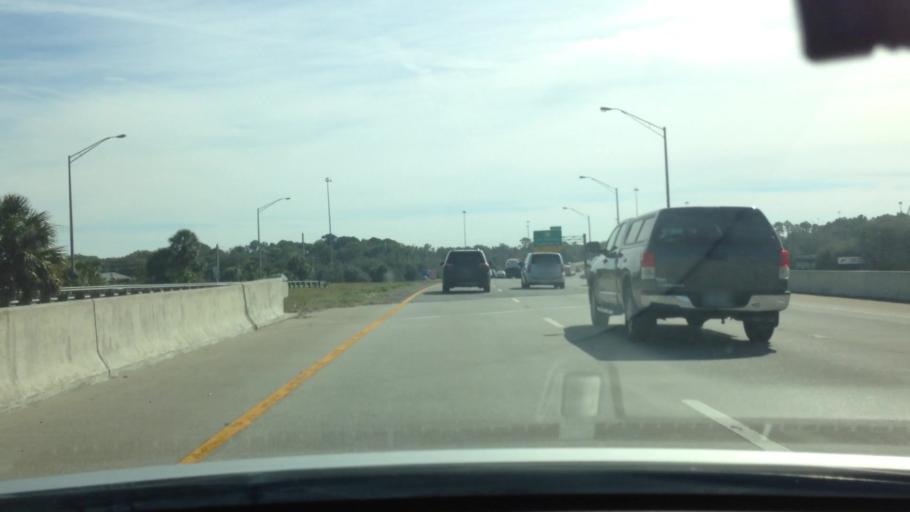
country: US
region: Florida
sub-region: Duval County
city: Jacksonville
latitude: 30.4202
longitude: -81.5649
